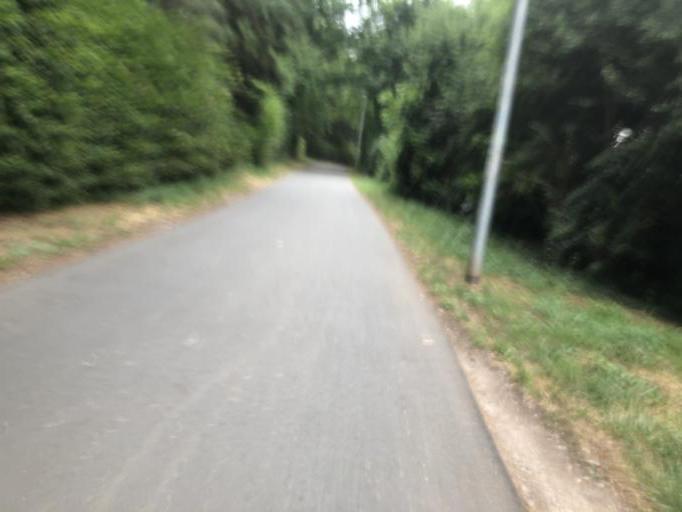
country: DE
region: Bavaria
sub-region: Regierungsbezirk Mittelfranken
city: Furth
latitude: 49.5049
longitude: 10.9758
